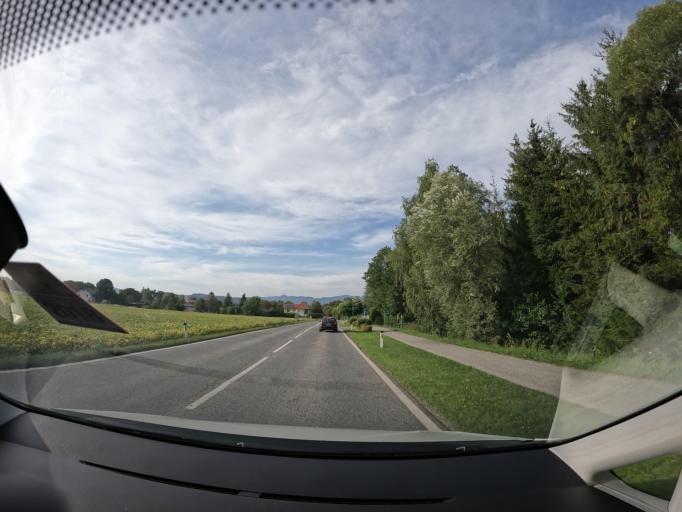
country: AT
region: Carinthia
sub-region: Politischer Bezirk Volkermarkt
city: Eberndorf
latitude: 46.6173
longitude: 14.6354
